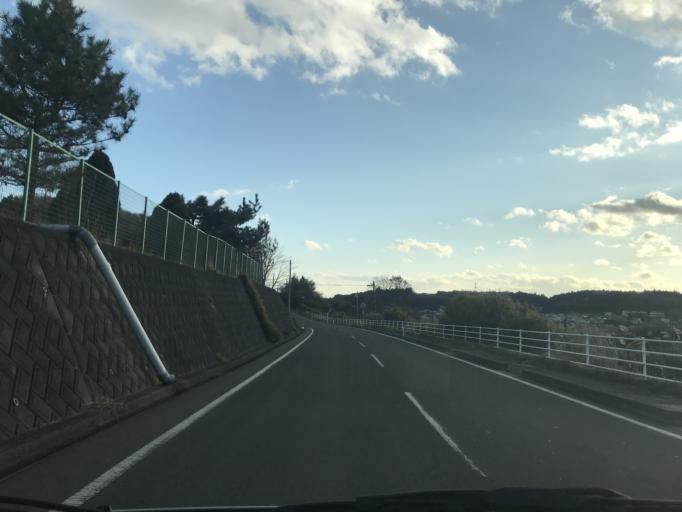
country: JP
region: Miyagi
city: Kogota
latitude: 38.6668
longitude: 141.0719
